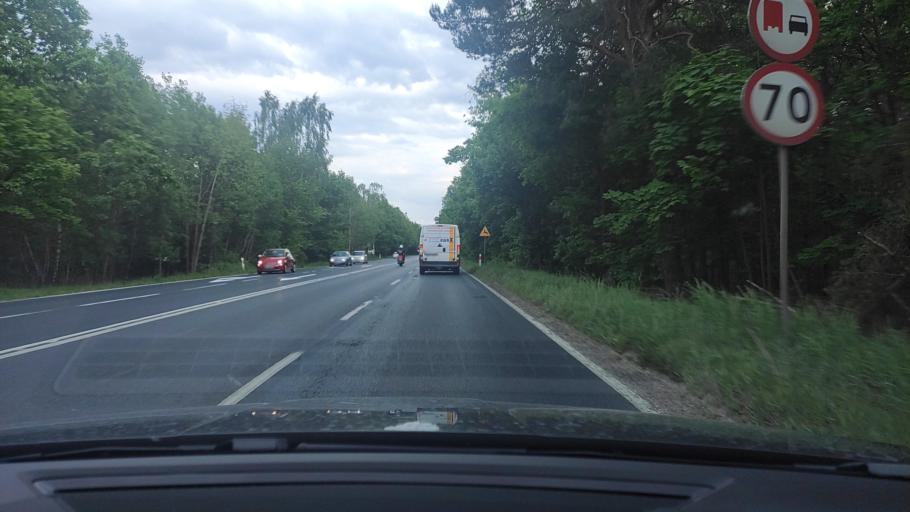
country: PL
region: Greater Poland Voivodeship
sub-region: Powiat poznanski
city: Czerwonak
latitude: 52.4264
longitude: 17.0131
